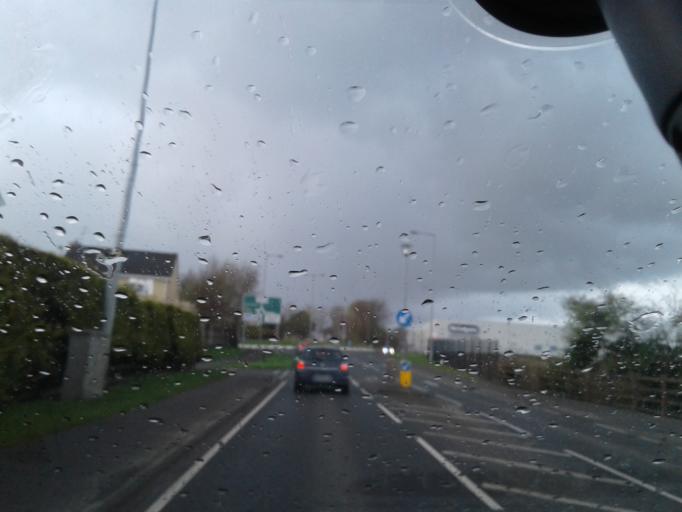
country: GB
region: Northern Ireland
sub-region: Strabane District
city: Strabane
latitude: 54.8059
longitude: -7.4730
